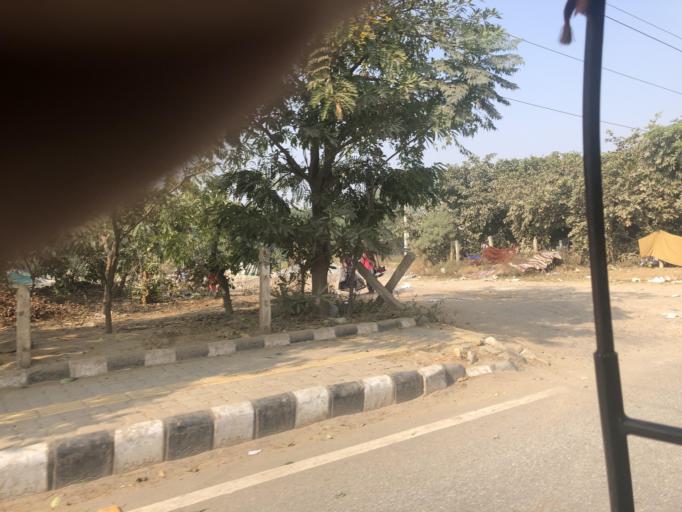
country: IN
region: Haryana
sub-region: Gurgaon
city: Gurgaon
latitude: 28.4275
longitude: 77.0912
